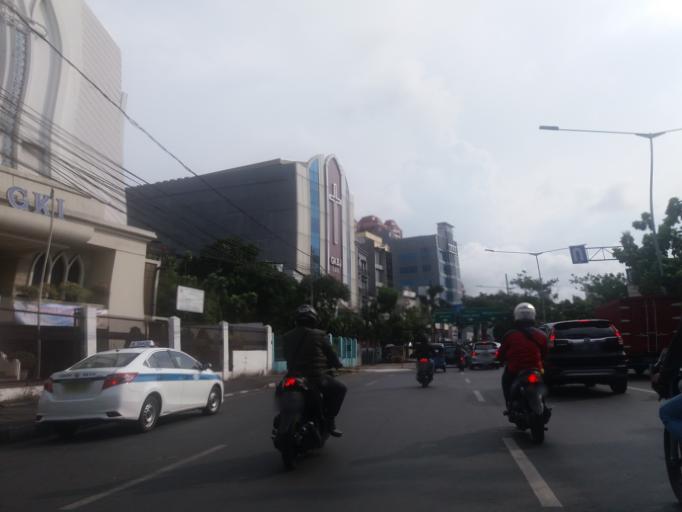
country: ID
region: Jakarta Raya
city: Jakarta
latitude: -6.1620
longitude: 106.8307
